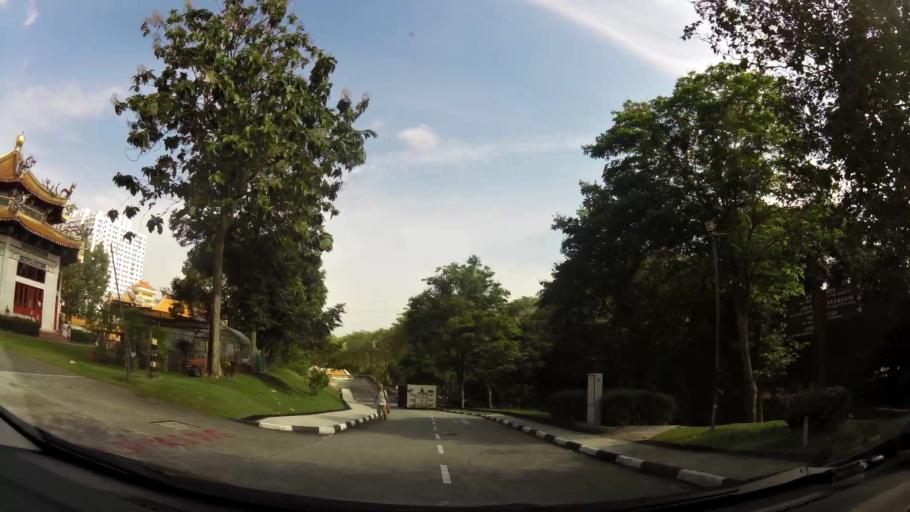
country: SG
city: Singapore
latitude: 1.3607
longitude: 103.8368
